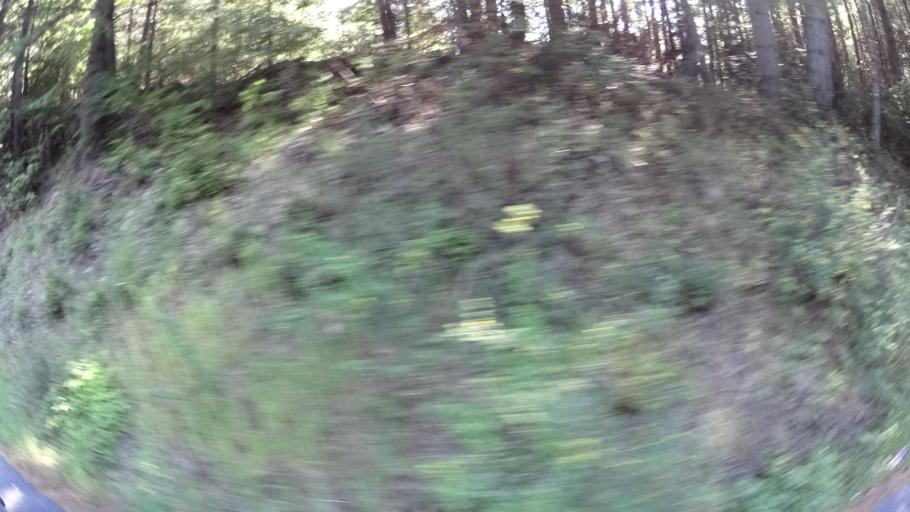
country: US
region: California
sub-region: Humboldt County
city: Rio Dell
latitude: 40.4594
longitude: -124.0073
